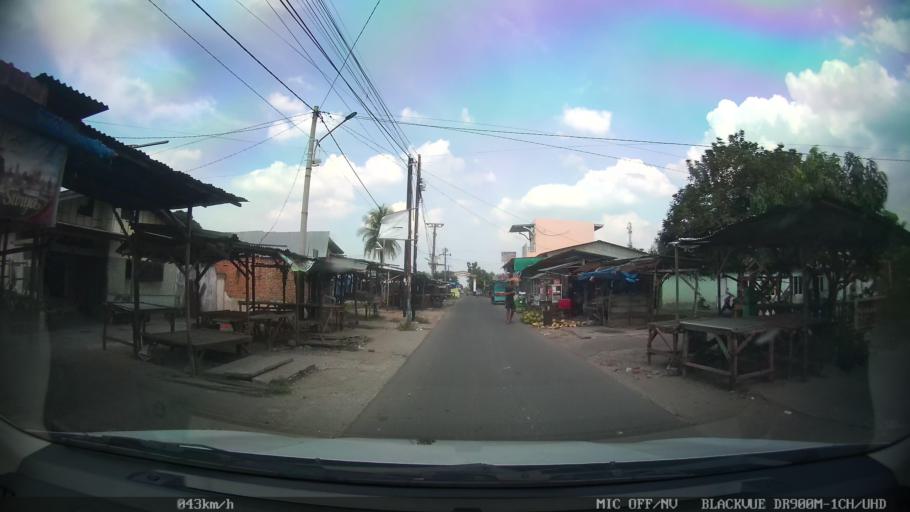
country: ID
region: North Sumatra
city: Binjai
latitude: 3.6132
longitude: 98.5252
